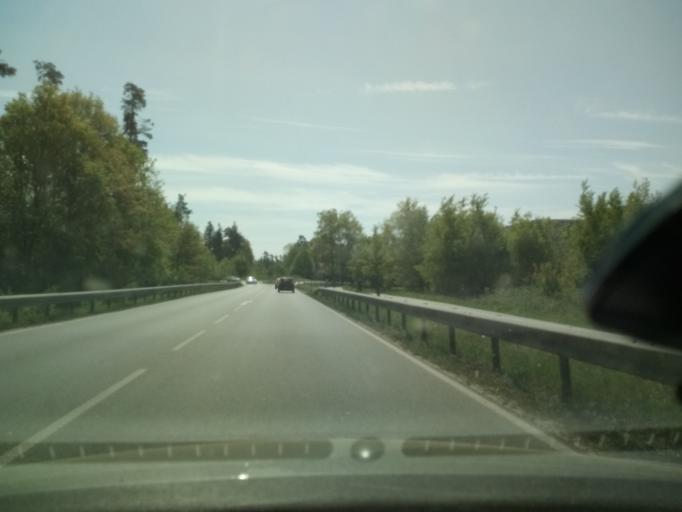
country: DE
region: Bavaria
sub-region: Upper Bavaria
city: Waldkraiburg
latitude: 48.2208
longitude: 12.4159
